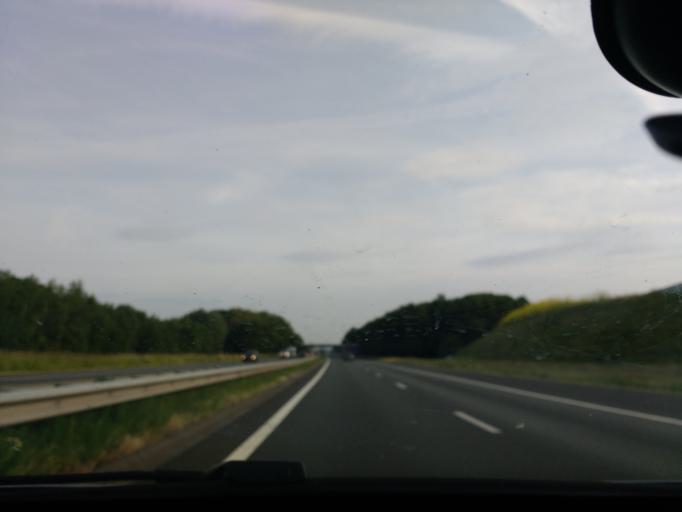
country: NL
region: Gelderland
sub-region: Gemeente Wijchen
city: Bergharen
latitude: 51.8299
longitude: 5.6837
